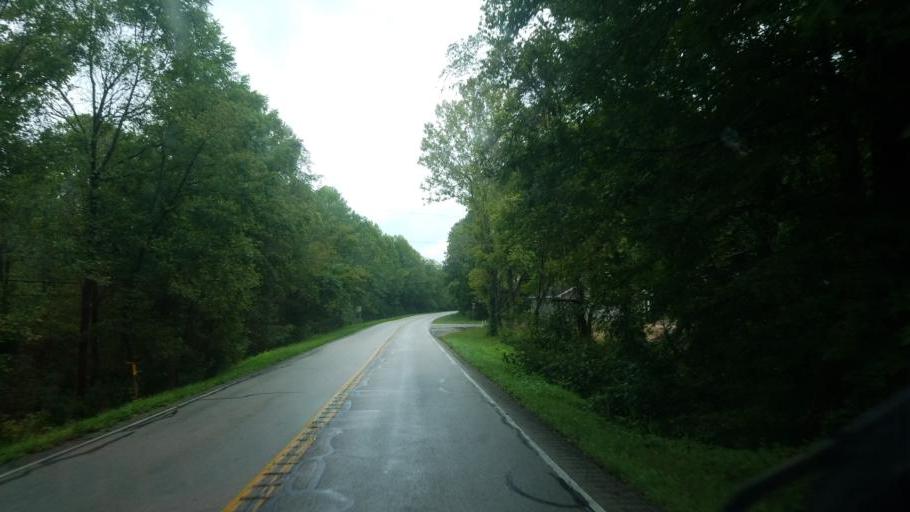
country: US
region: Kentucky
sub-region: Rowan County
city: Morehead
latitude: 38.1511
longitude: -83.4879
